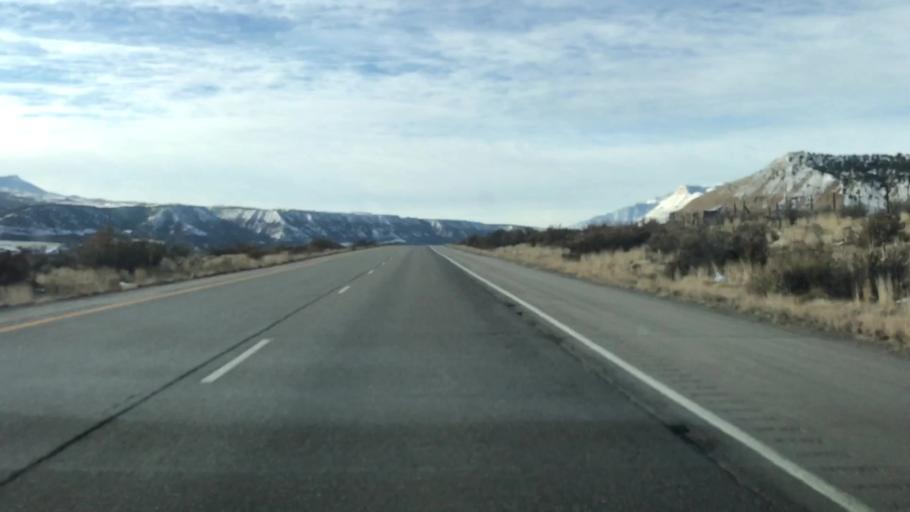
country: US
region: Colorado
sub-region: Garfield County
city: Battlement Mesa
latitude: 39.4931
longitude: -107.9491
